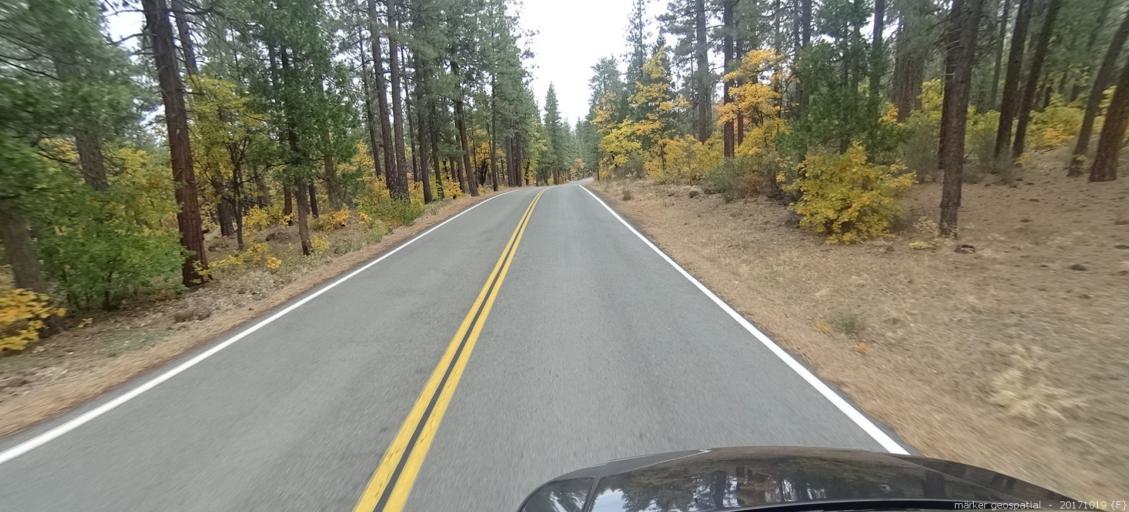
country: US
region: California
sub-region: Shasta County
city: Burney
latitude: 41.1800
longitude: -121.3628
